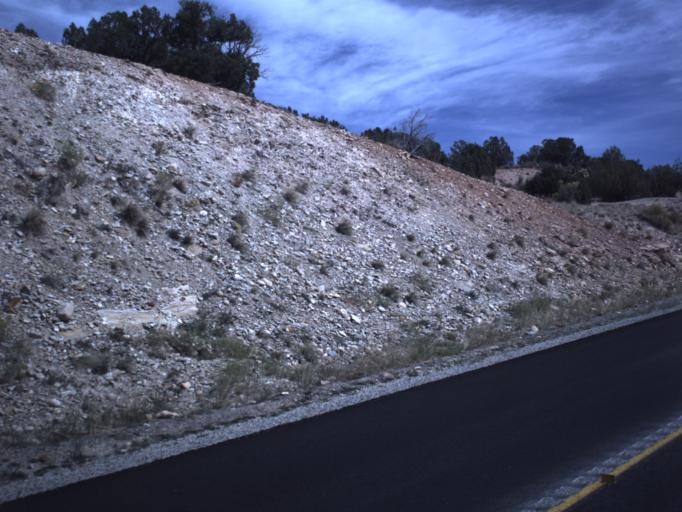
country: US
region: Utah
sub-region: San Juan County
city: Blanding
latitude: 37.5762
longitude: -109.5293
